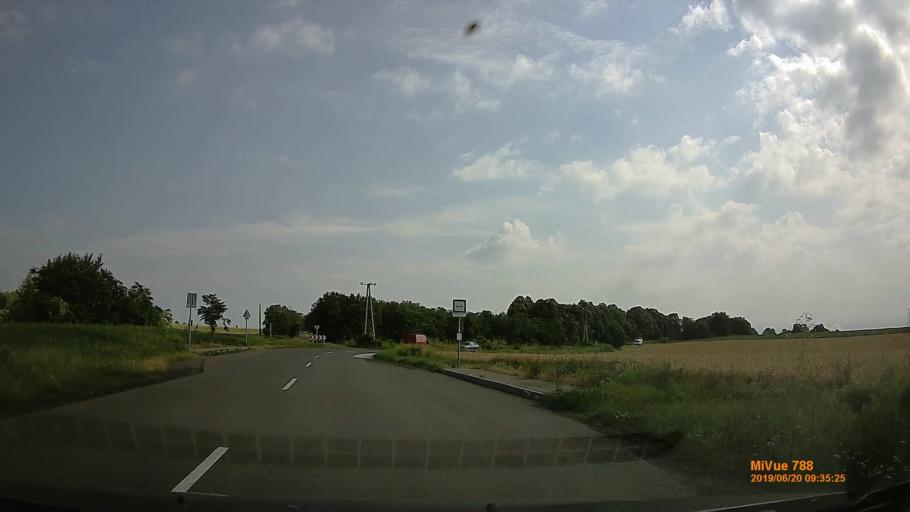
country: HU
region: Baranya
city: Pecsvarad
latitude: 46.1642
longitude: 18.4372
